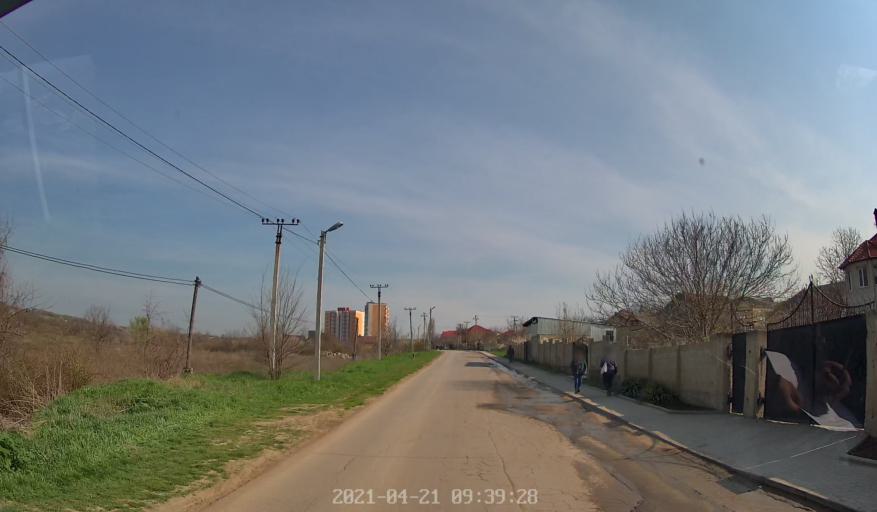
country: MD
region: Chisinau
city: Chisinau
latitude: 46.9895
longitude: 28.9336
